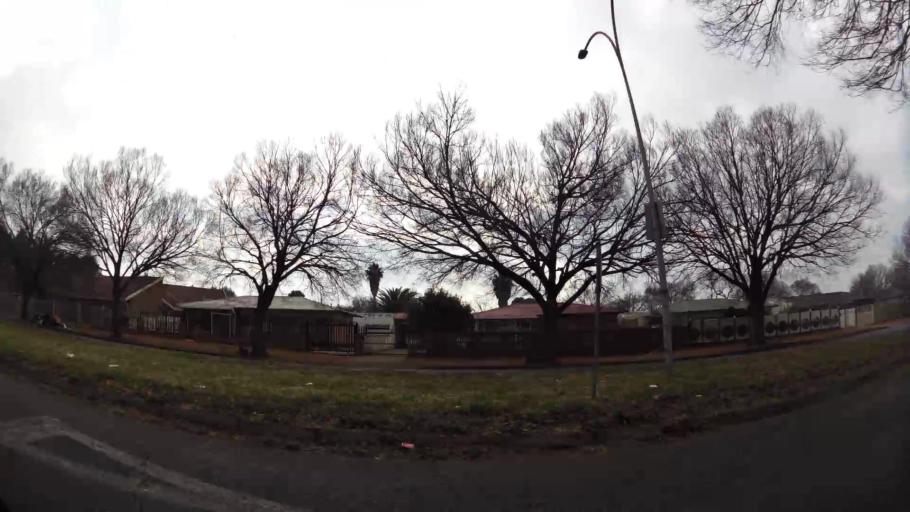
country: ZA
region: Gauteng
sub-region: Sedibeng District Municipality
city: Vanderbijlpark
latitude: -26.6893
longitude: 27.8263
